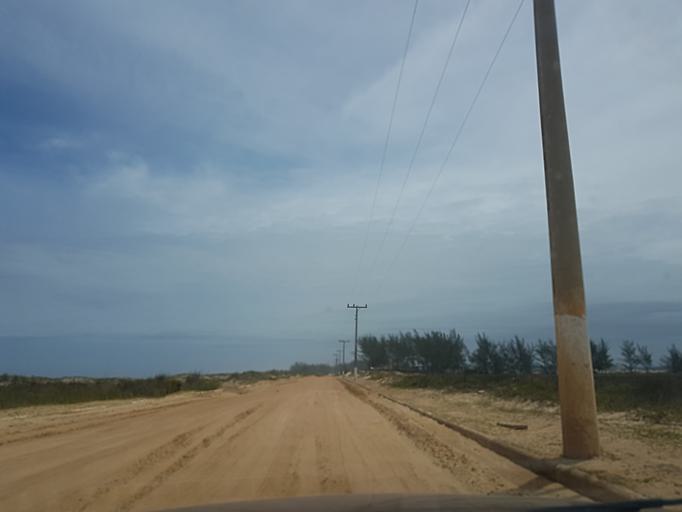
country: BR
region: Santa Catarina
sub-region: Jaguaruna
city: Jaguaruna
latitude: -28.6674
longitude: -48.9687
